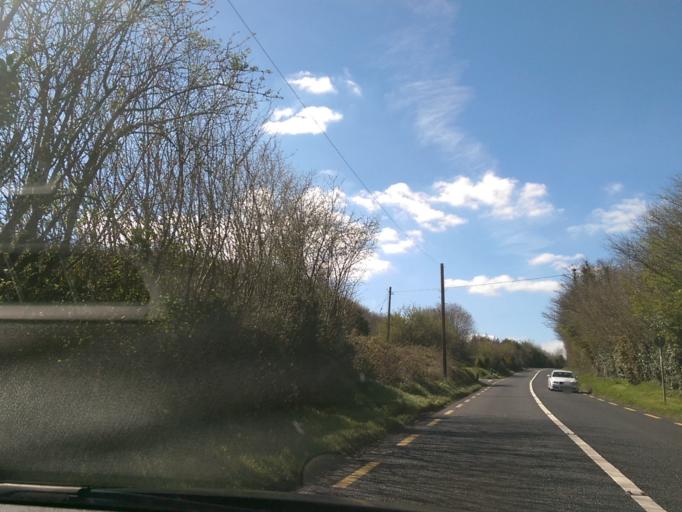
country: IE
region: Leinster
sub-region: Laois
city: Stradbally
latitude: 53.0252
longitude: -7.1964
